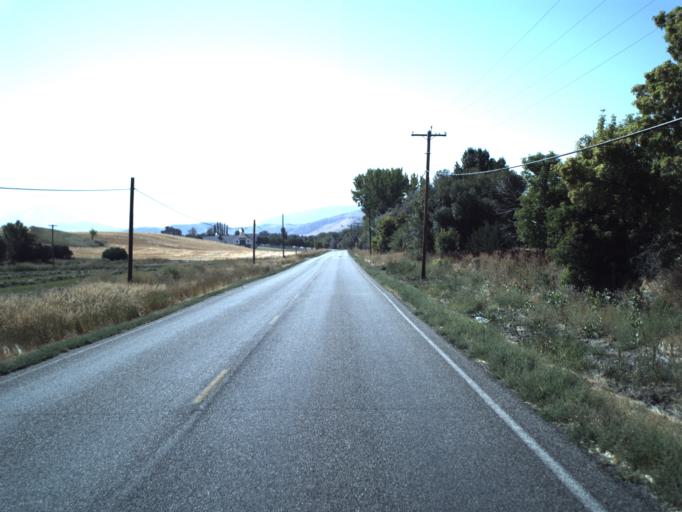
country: US
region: Utah
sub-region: Cache County
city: Hyrum
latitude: 41.5875
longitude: -111.8378
